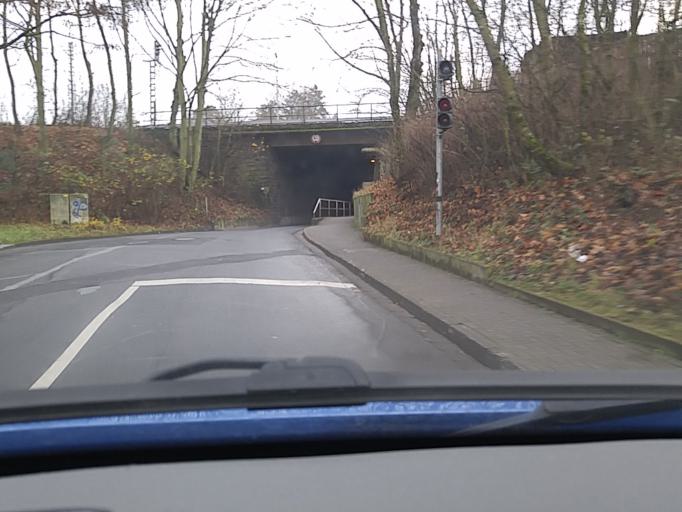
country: DE
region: Hesse
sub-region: Regierungsbezirk Darmstadt
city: Bad Nauheim
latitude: 50.3714
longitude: 8.7474
